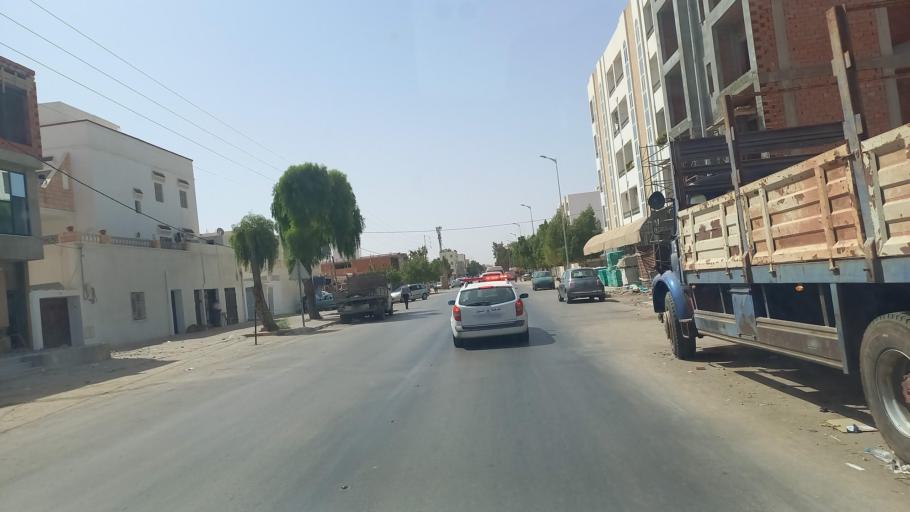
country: TN
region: Madanin
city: Medenine
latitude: 33.3314
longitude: 10.4853
